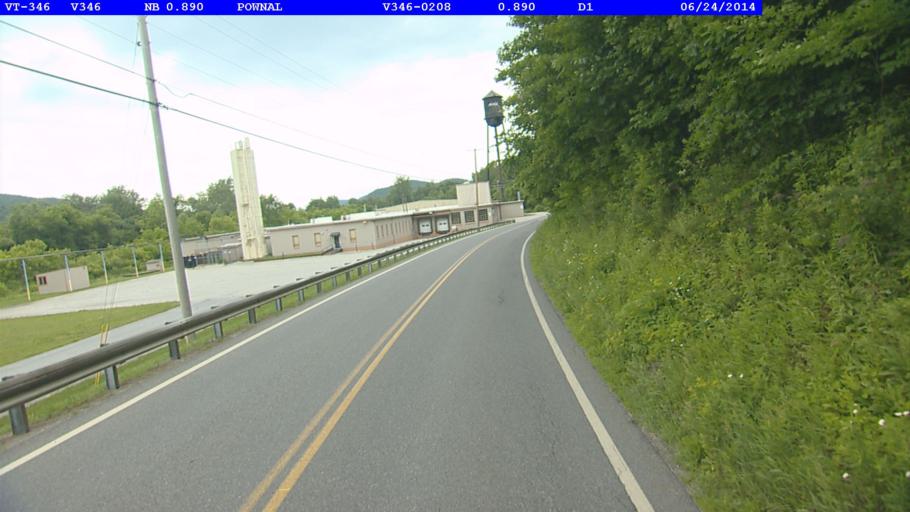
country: US
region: Massachusetts
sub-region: Berkshire County
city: Williamstown
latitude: 42.7736
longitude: -73.2412
